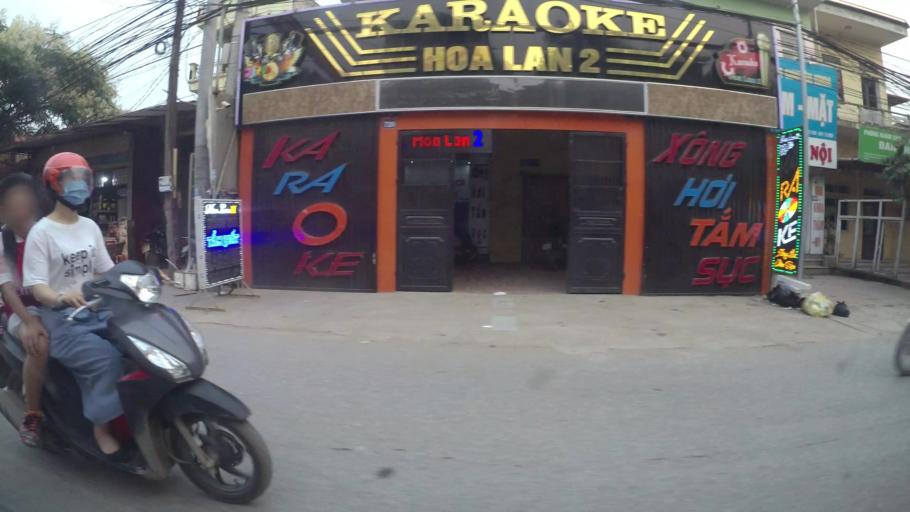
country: VN
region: Ha Noi
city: Ha Dong
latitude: 20.9920
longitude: 105.7310
